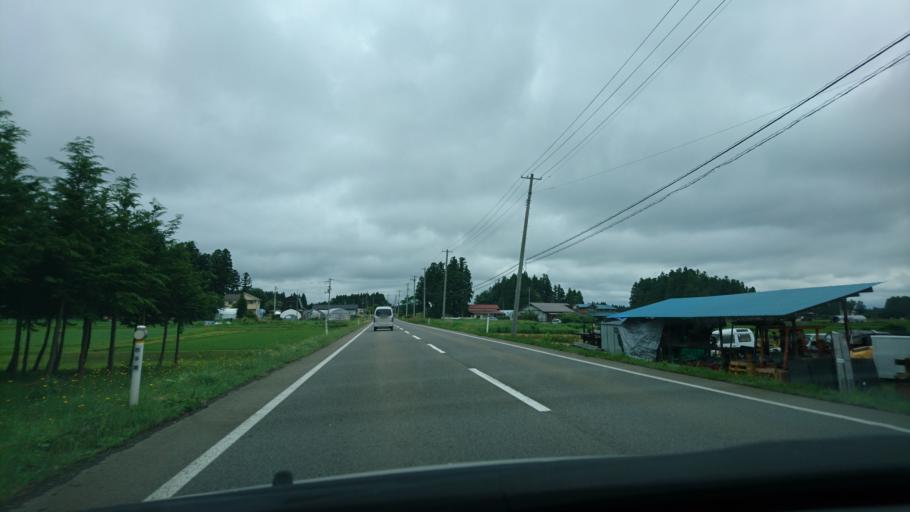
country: JP
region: Iwate
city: Mizusawa
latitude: 39.1085
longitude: 141.0525
